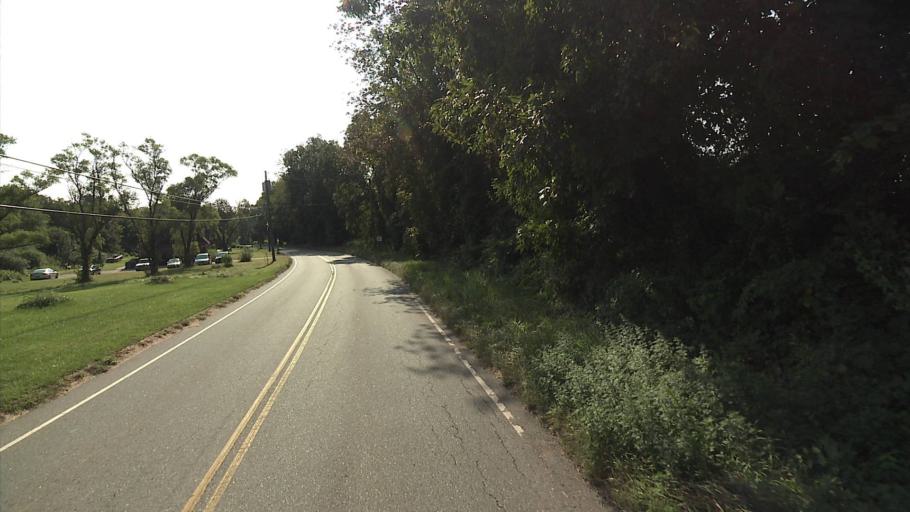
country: US
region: Connecticut
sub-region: Windham County
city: South Windham
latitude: 41.6154
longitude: -72.1924
